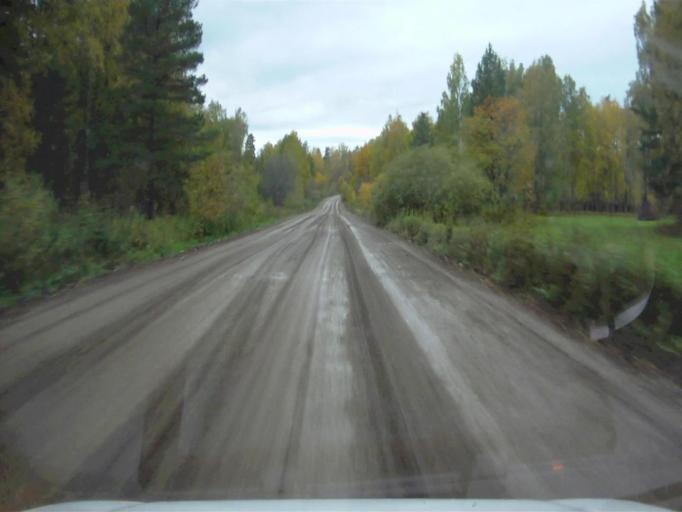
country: RU
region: Chelyabinsk
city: Nyazepetrovsk
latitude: 56.1088
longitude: 59.3772
